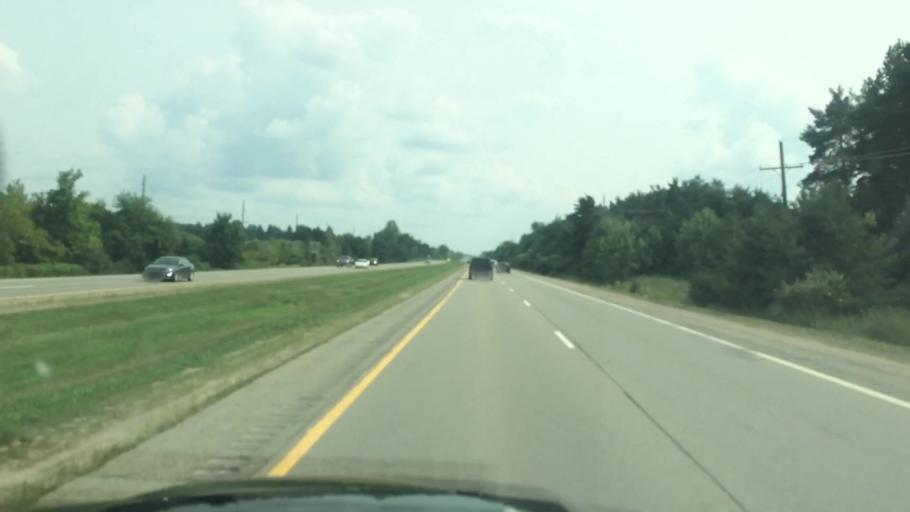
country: US
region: Michigan
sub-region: Oakland County
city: Oxford
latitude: 42.8672
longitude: -83.2945
